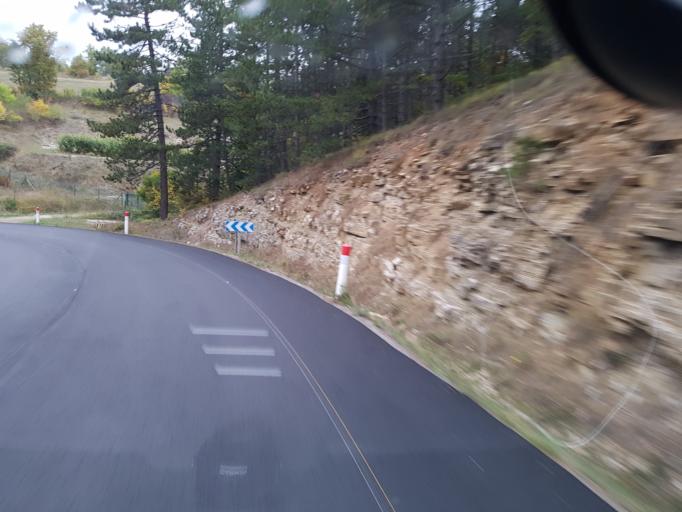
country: FR
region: Languedoc-Roussillon
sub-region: Departement de la Lozere
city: Mende
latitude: 44.5372
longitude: 3.5832
